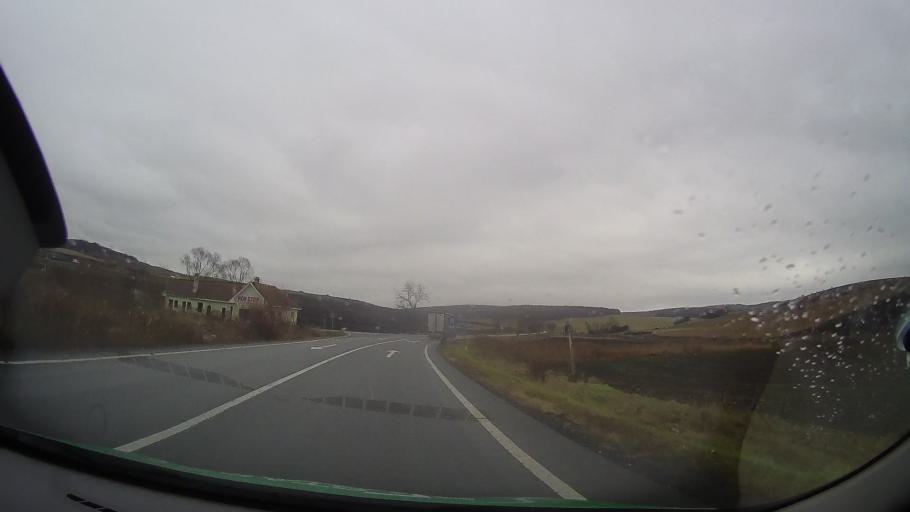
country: RO
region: Mures
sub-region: Comuna Lunca
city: Lunca
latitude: 46.8694
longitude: 24.5532
